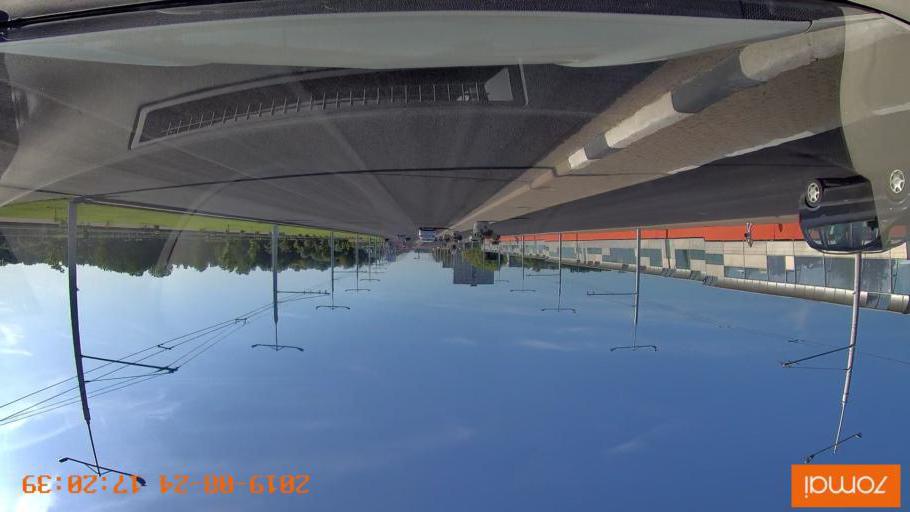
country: BY
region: Minsk
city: Hatava
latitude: 53.8524
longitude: 27.6328
